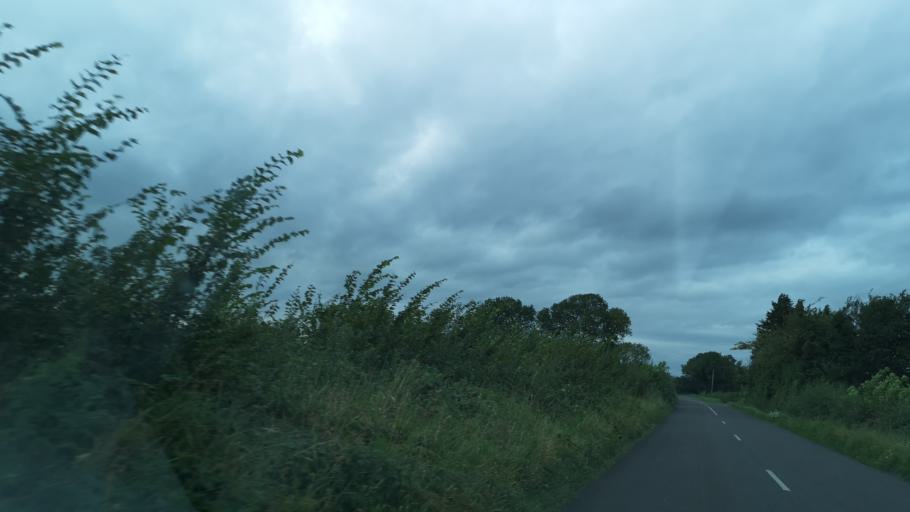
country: IE
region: Leinster
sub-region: Uibh Fhaili
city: Ferbane
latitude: 53.2156
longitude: -7.7913
